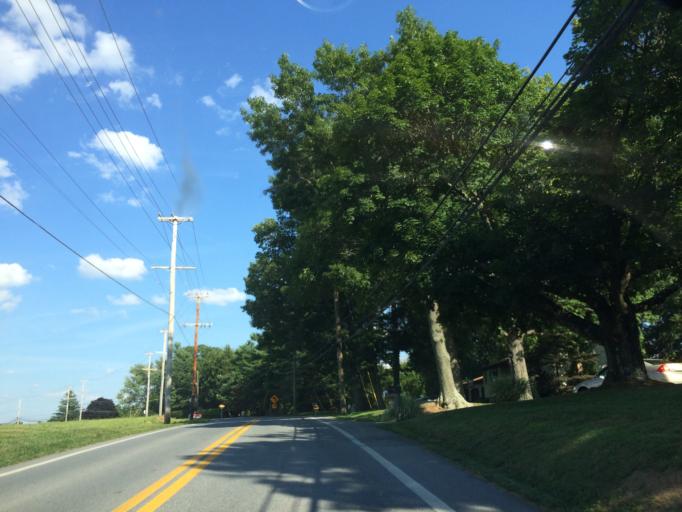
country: US
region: Maryland
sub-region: Carroll County
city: Sykesville
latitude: 39.3800
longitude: -76.9888
